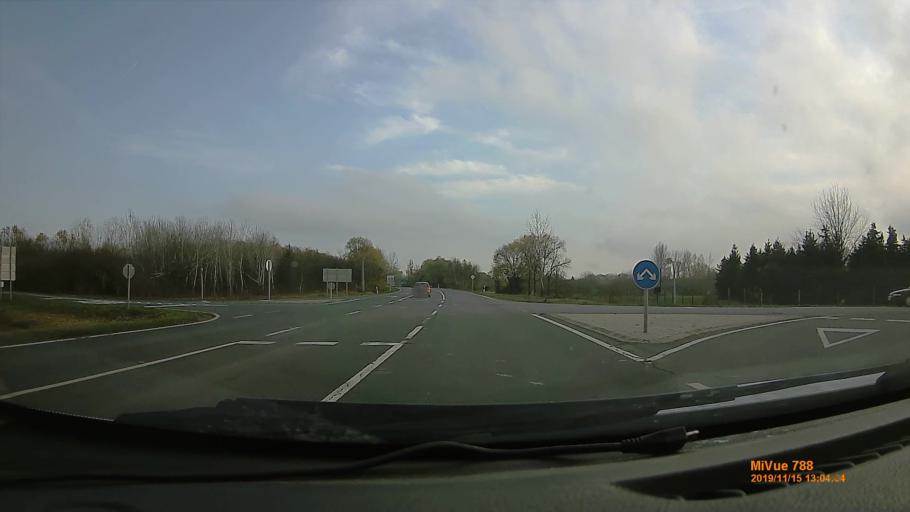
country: HU
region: Bekes
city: Gyula
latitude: 46.6376
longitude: 21.2497
